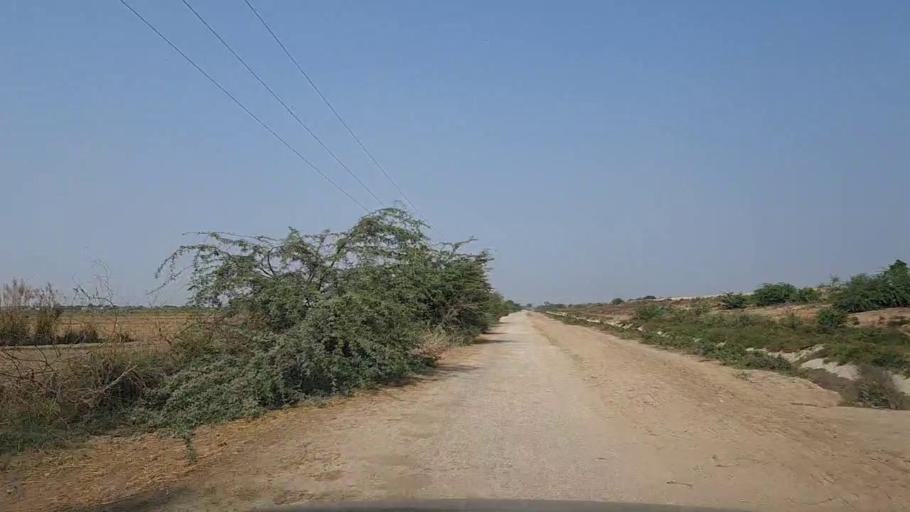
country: PK
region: Sindh
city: Chuhar Jamali
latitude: 24.5149
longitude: 67.9250
